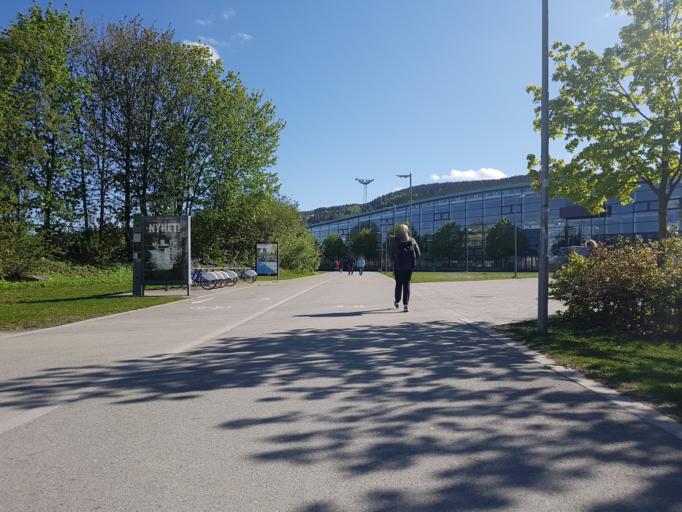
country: NO
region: Buskerud
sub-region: Drammen
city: Drammen
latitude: 59.7372
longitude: 10.2004
